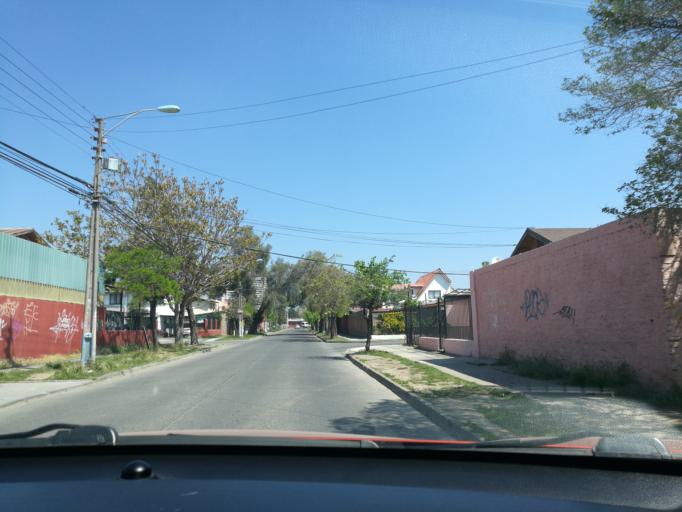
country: CL
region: O'Higgins
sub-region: Provincia de Cachapoal
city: Rancagua
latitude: -34.1614
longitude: -70.7361
